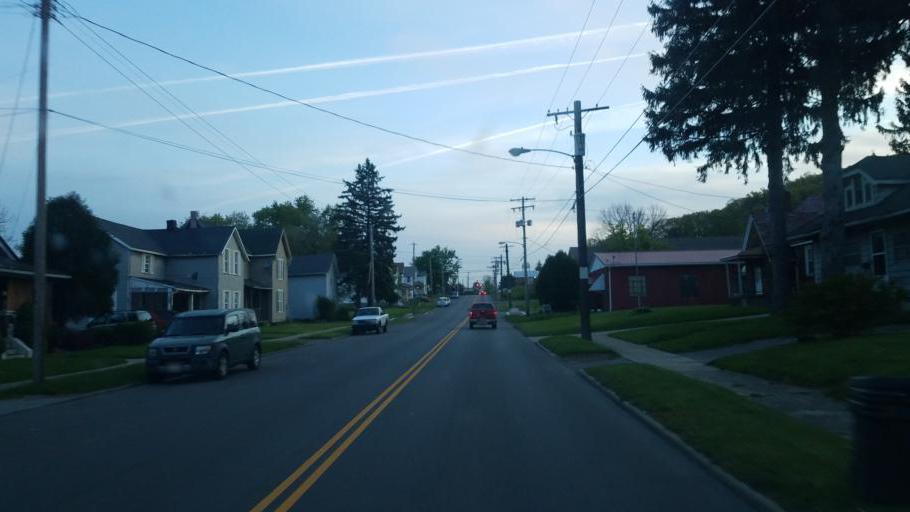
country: US
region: Ohio
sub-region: Richland County
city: Mansfield
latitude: 40.7719
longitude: -82.5066
